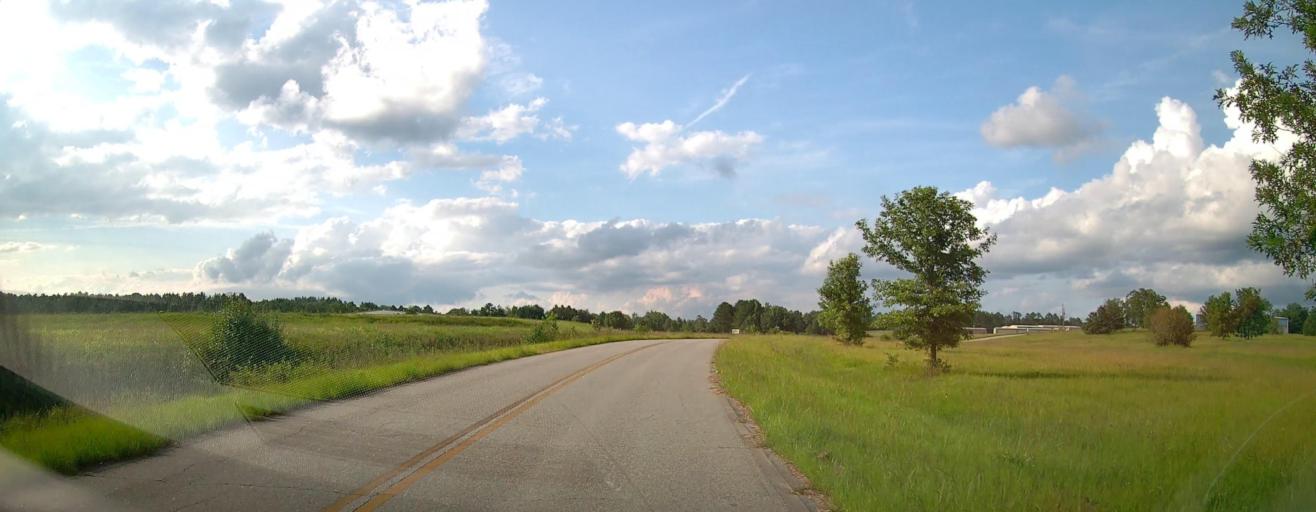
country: US
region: Georgia
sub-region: Crawford County
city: Roberta
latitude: 32.7145
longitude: -84.0231
